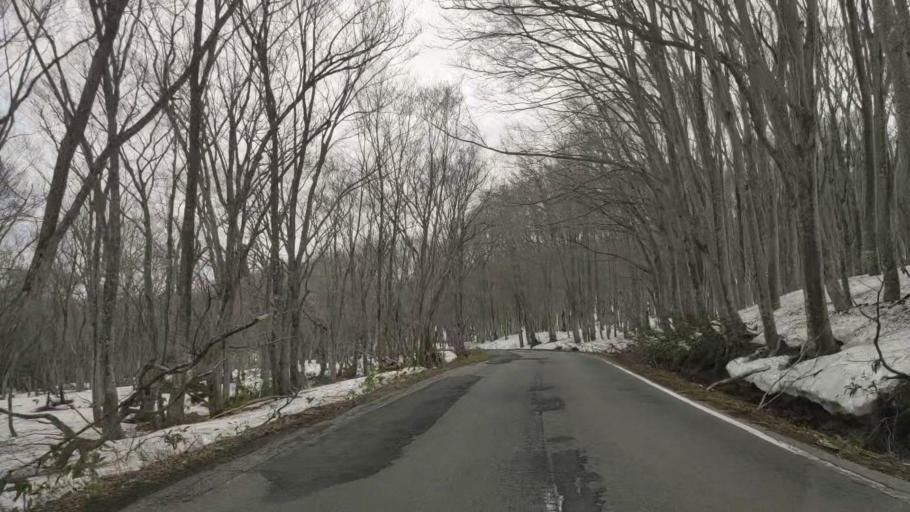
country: JP
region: Aomori
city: Aomori Shi
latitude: 40.6987
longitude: 140.9029
